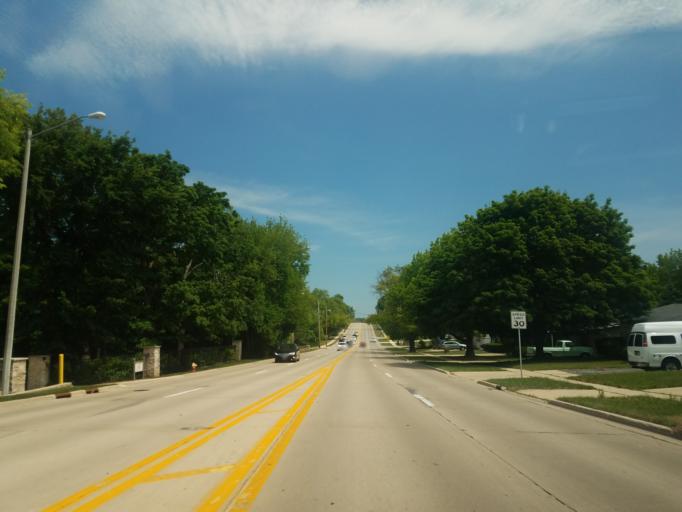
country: US
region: Illinois
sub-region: McLean County
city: Bloomington
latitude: 40.4942
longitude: -88.9642
